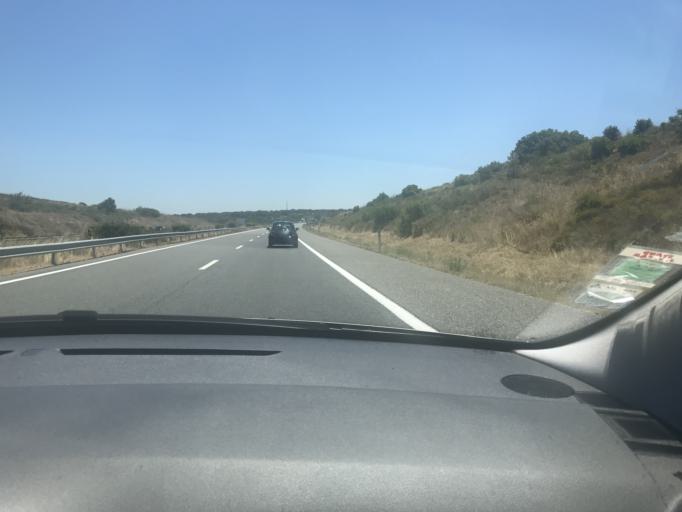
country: PT
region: Setubal
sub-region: Grandola
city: Grandola
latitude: 38.1314
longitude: -8.4248
